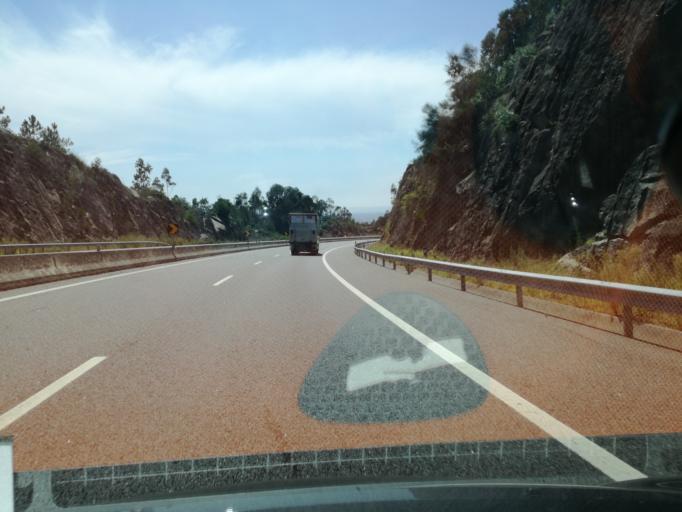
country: PT
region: Viana do Castelo
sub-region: Viana do Castelo
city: Meadela
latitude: 41.7401
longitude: -8.7919
